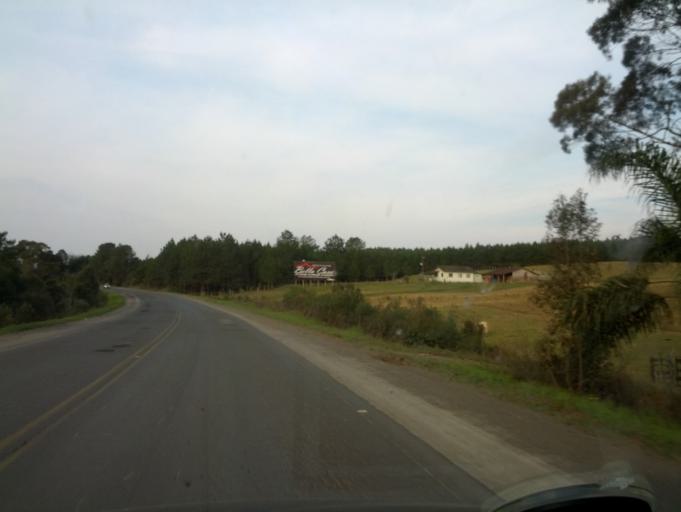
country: BR
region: Santa Catarina
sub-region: Otacilio Costa
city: Otacilio Costa
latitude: -27.3098
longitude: -50.1195
